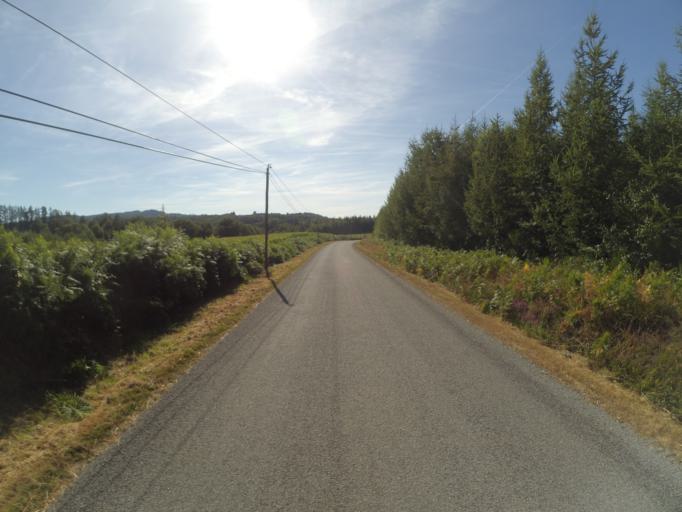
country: FR
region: Limousin
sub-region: Departement de la Haute-Vienne
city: Eymoutiers
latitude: 45.7112
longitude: 1.8604
